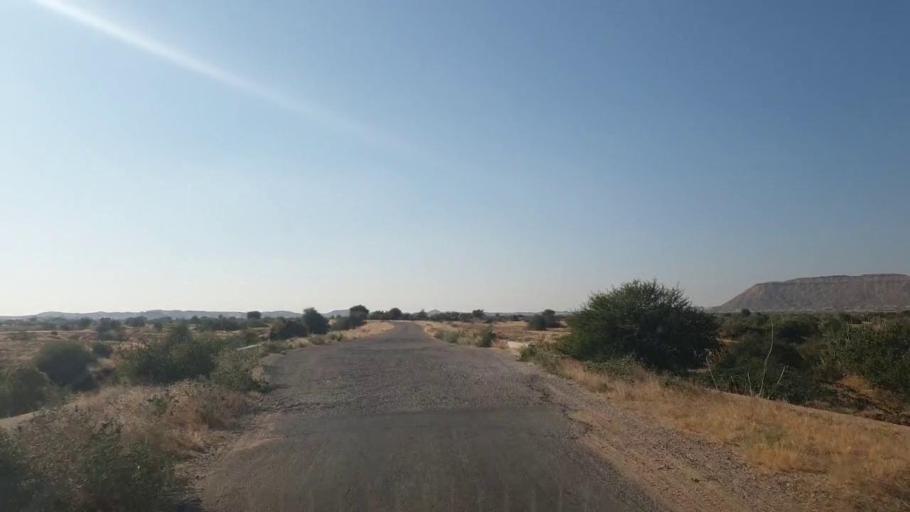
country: PK
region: Sindh
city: Malir Cantonment
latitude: 25.3890
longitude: 67.5239
